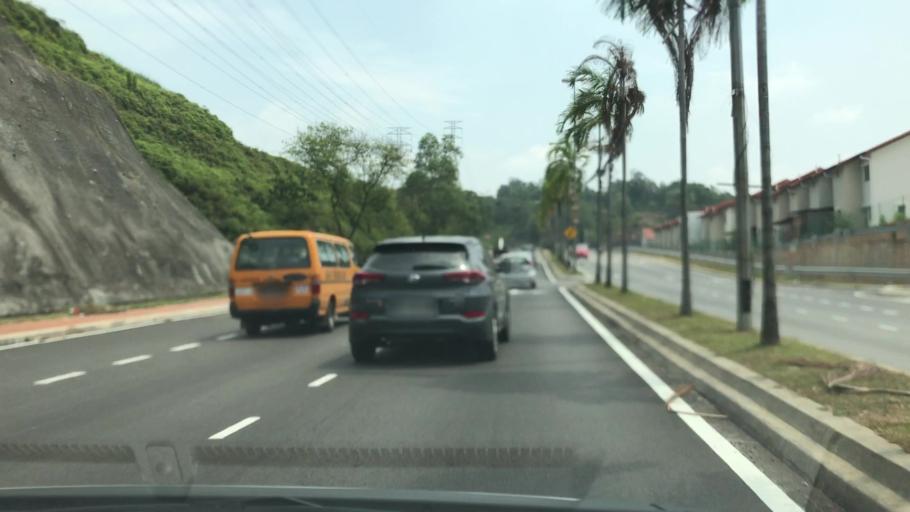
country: MY
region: Selangor
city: Kampong Baharu Balakong
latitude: 3.0376
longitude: 101.6764
